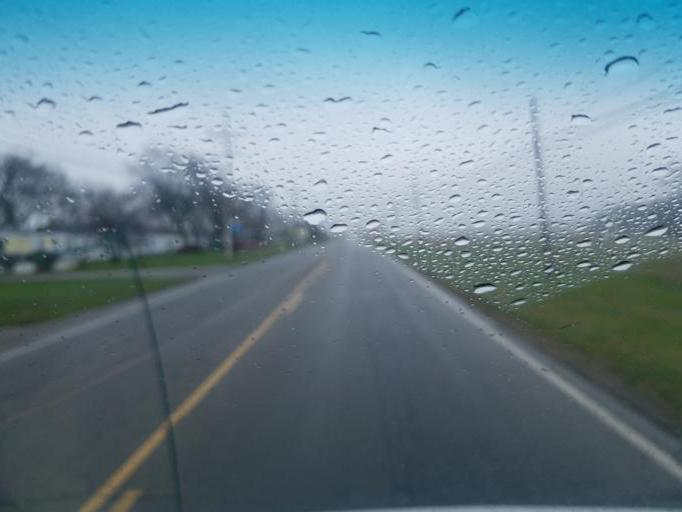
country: US
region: Ohio
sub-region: Hancock County
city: Findlay
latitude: 41.1055
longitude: -83.6498
